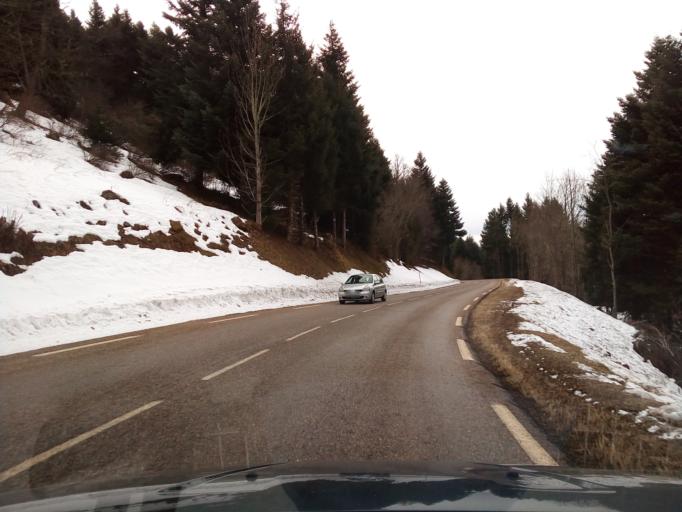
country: FR
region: Rhone-Alpes
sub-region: Departement de l'Isere
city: Revel
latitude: 45.1451
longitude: 5.8780
